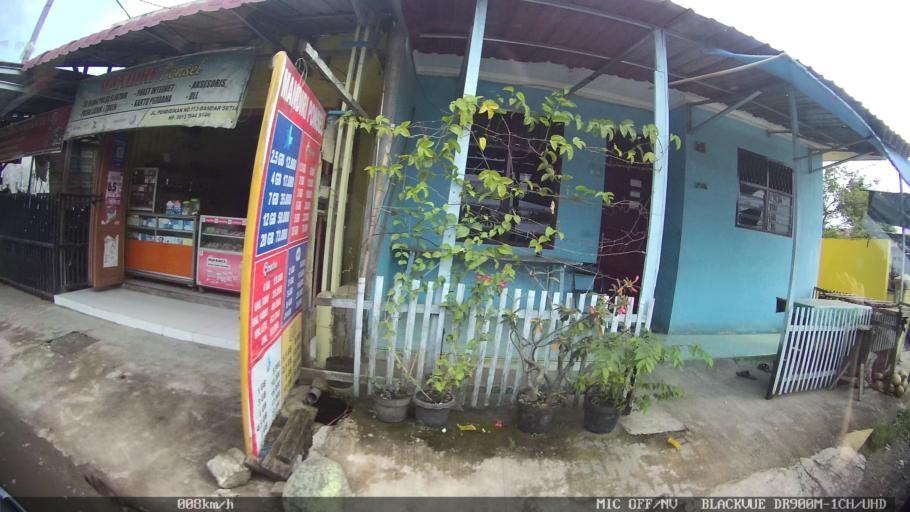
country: ID
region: North Sumatra
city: Medan
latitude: 3.6202
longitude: 98.7518
